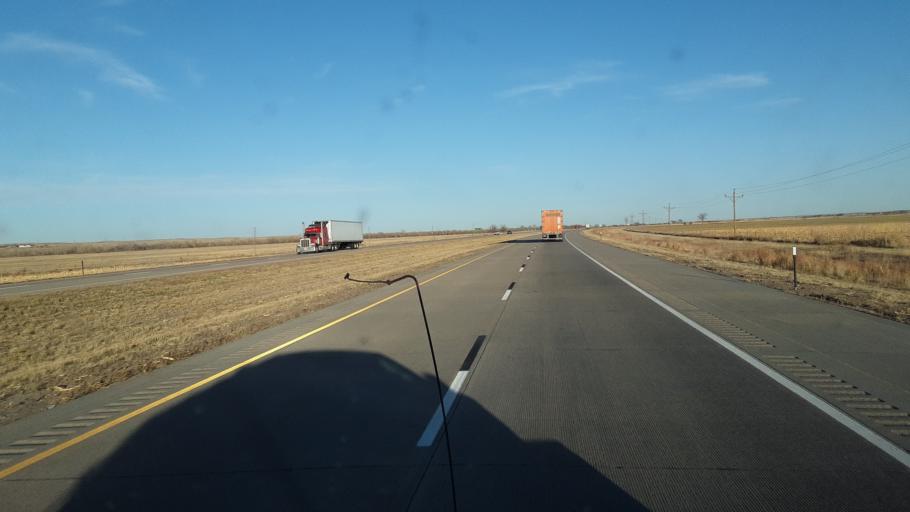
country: US
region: Colorado
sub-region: Sedgwick County
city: Julesburg
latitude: 41.0601
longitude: -102.0317
